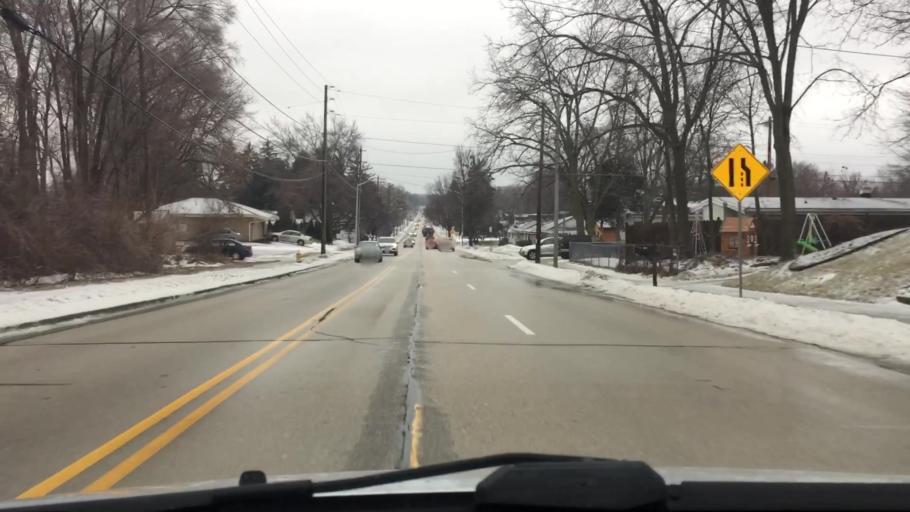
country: US
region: Wisconsin
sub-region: Waukesha County
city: Waukesha
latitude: 43.0305
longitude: -88.2559
